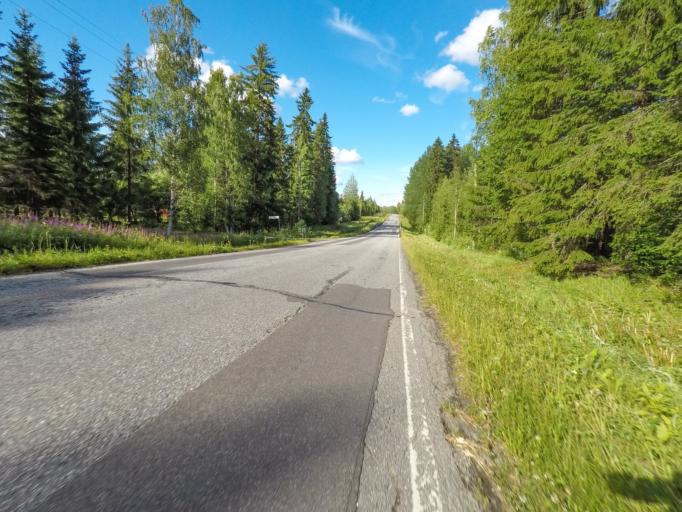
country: FI
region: South Karelia
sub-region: Imatra
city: Imatra
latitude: 61.1356
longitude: 28.7331
